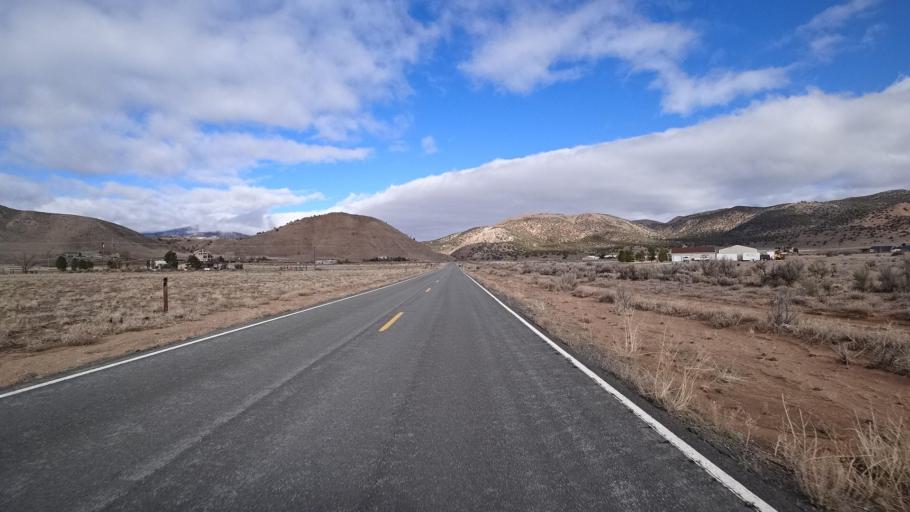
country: US
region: Nevada
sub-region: Washoe County
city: Cold Springs
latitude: 39.8938
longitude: -119.9793
